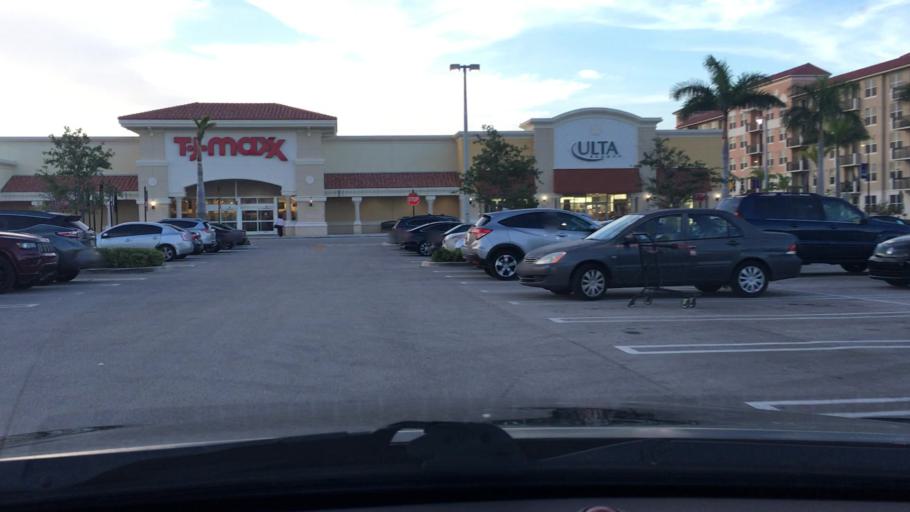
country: US
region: Florida
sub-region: Miami-Dade County
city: Fountainebleau
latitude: 25.7706
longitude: -80.3586
